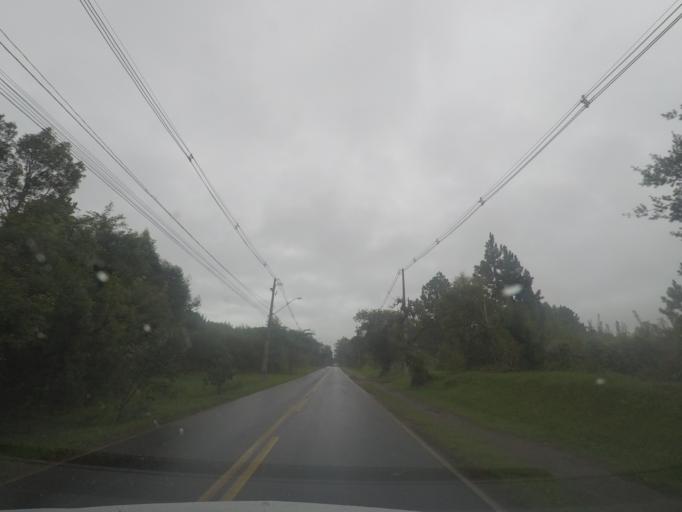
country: BR
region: Parana
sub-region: Quatro Barras
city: Quatro Barras
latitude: -25.3720
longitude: -49.0871
